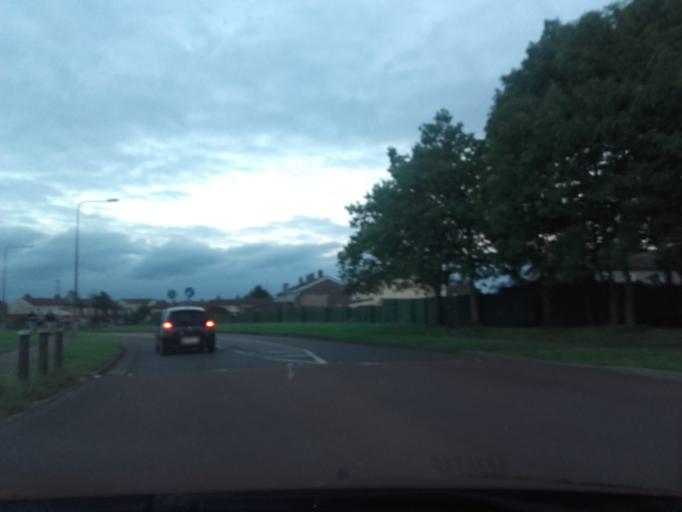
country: IE
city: Jobstown
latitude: 53.2890
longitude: -6.3990
